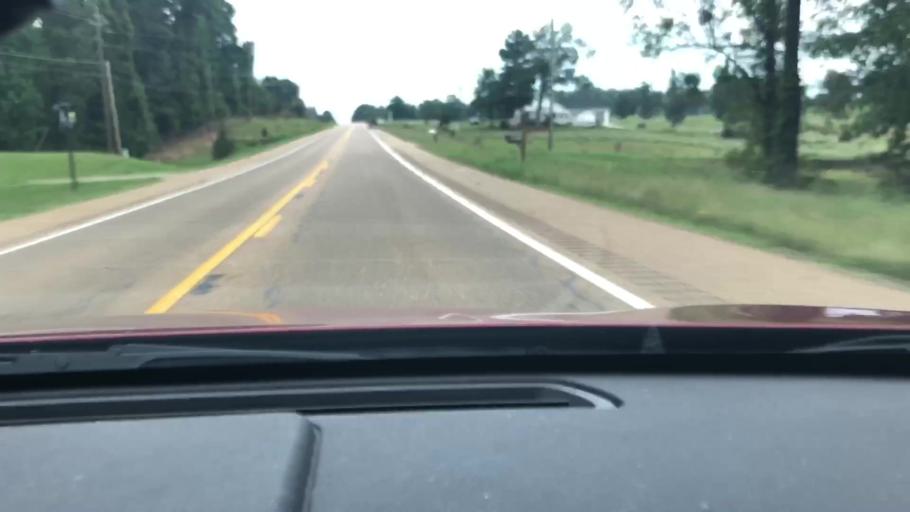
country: US
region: Arkansas
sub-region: Miller County
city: Texarkana
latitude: 33.4292
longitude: -93.9338
